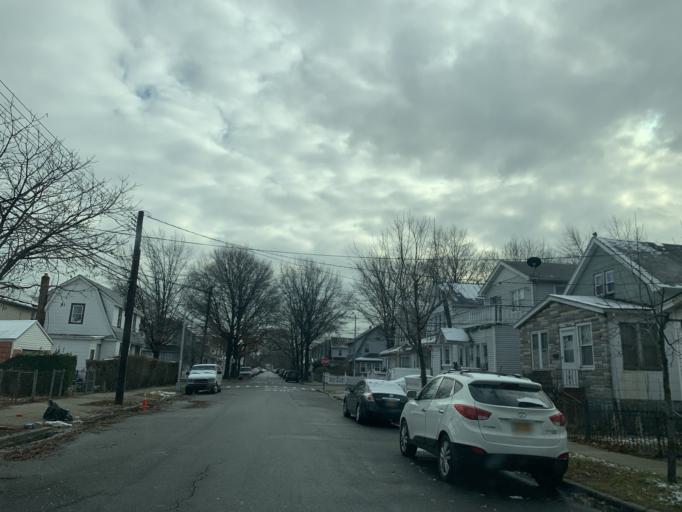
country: US
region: New York
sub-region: Queens County
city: Jamaica
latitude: 40.6896
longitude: -73.7810
